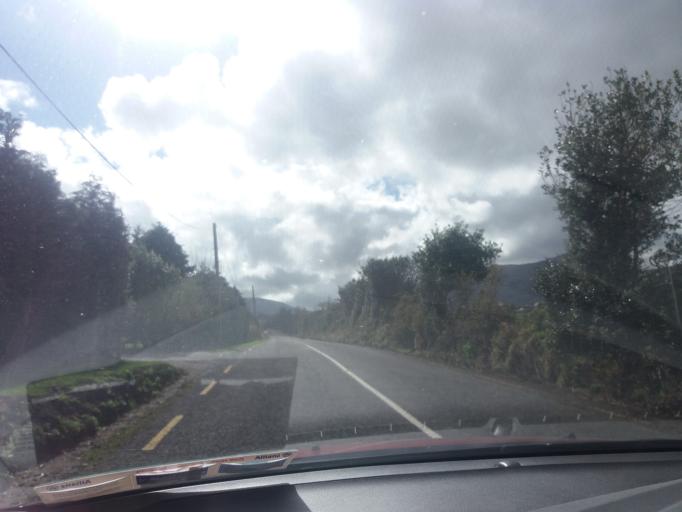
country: IE
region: Munster
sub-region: Ciarrai
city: Dingle
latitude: 52.2152
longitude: -10.1573
